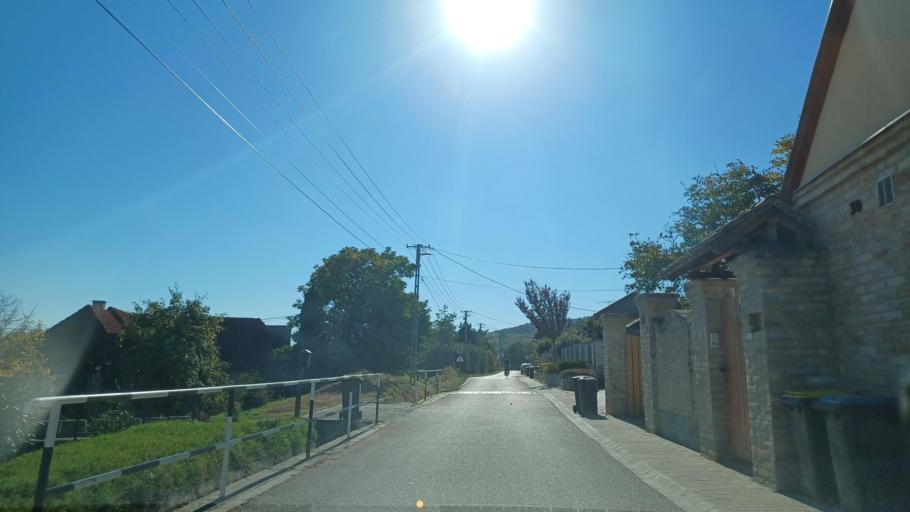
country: HU
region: Tolna
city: Szekszard
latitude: 46.3123
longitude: 18.6915
